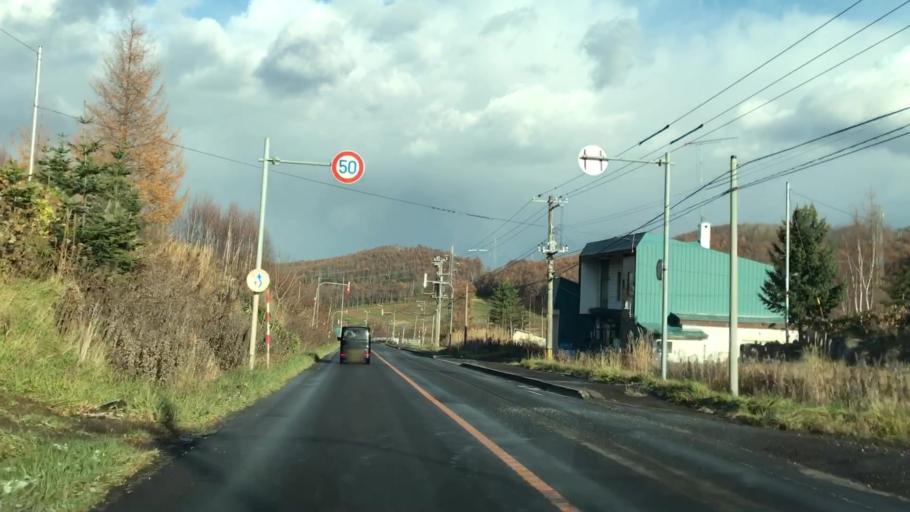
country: JP
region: Hokkaido
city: Otaru
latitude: 43.1903
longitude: 140.9587
